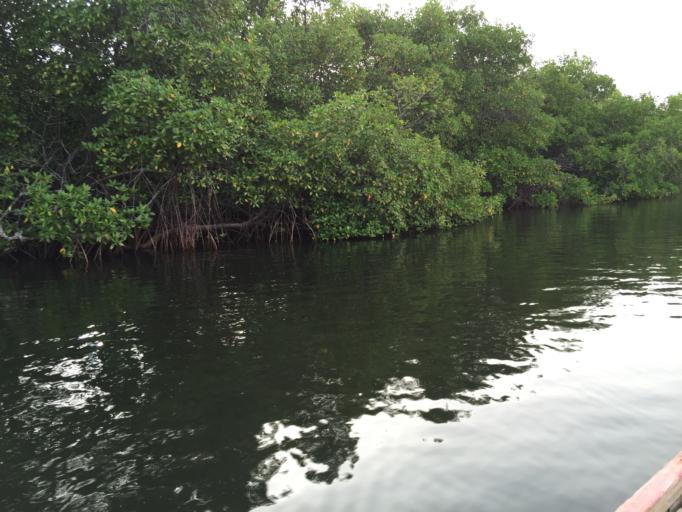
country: SN
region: Fatick
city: Sokone
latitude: 13.7616
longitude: -16.4938
